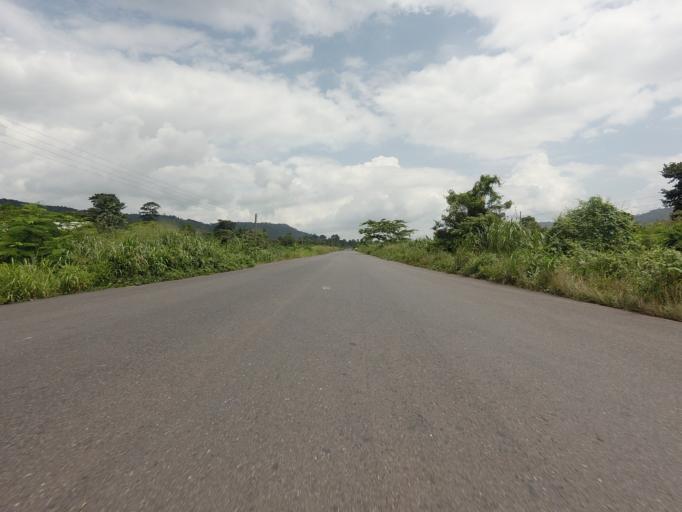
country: GH
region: Volta
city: Ho
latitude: 6.5491
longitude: 0.2541
